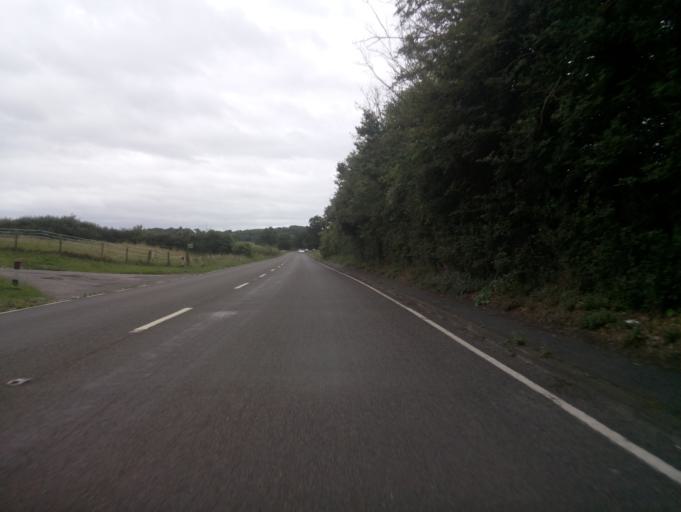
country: GB
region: England
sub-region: Worcestershire
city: Fernhill Heath
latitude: 52.2362
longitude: -2.1772
